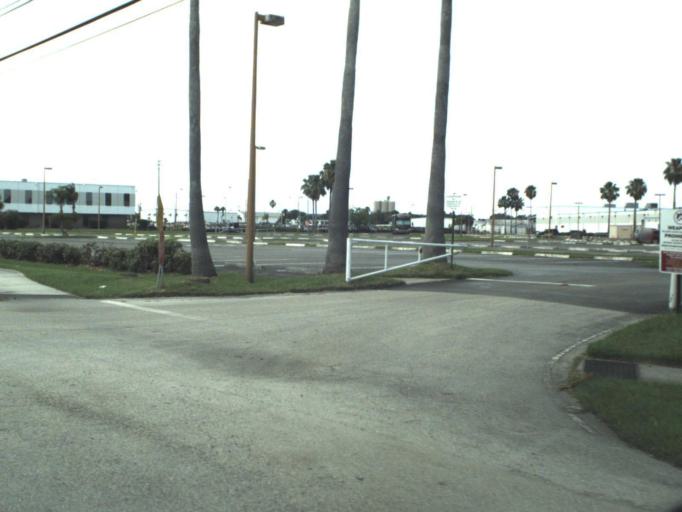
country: US
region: Florida
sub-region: Brevard County
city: Cape Canaveral
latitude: 28.3932
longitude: -80.6094
